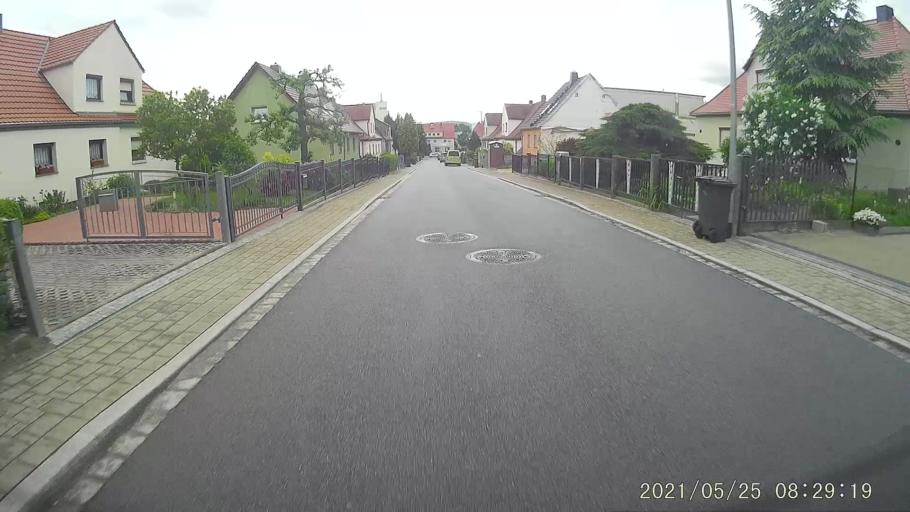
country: DE
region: Saxony
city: Bautzen
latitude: 51.1775
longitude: 14.4539
